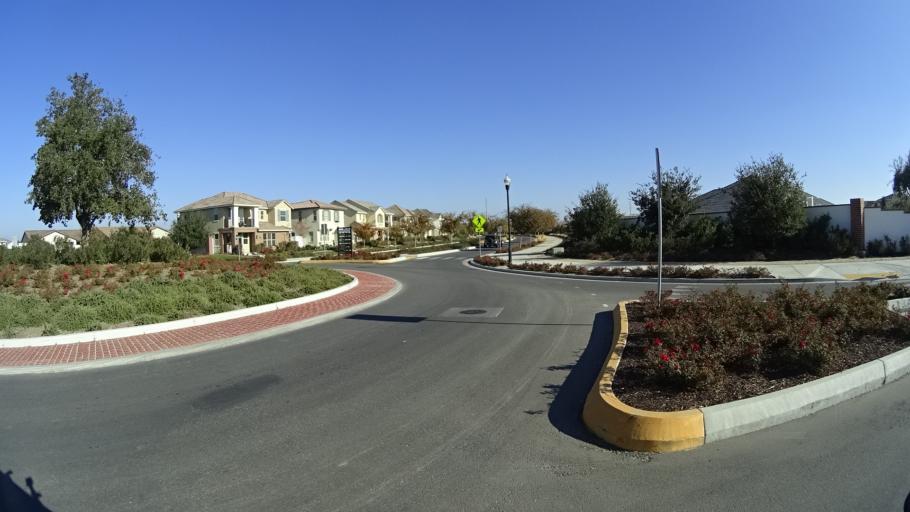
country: US
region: California
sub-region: Kern County
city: Rosedale
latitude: 35.3181
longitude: -119.1326
